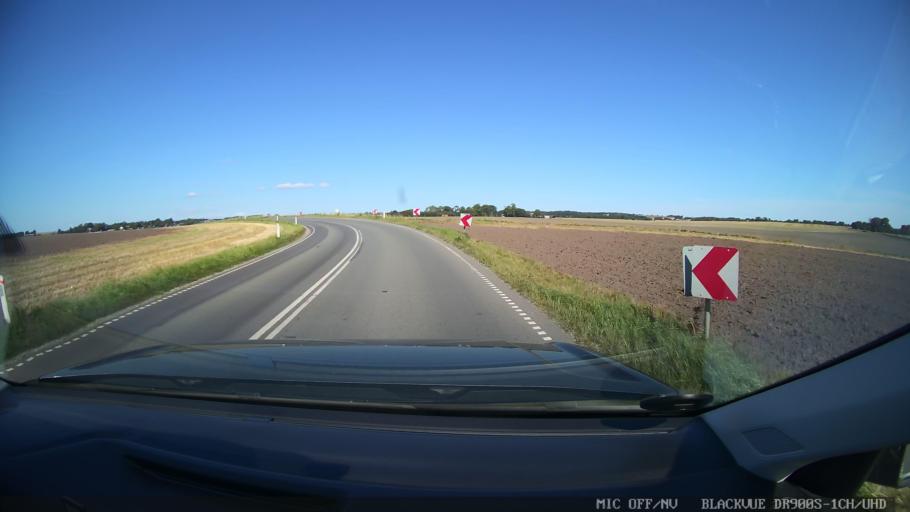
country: DK
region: Central Jutland
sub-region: Randers Kommune
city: Spentrup
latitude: 56.5446
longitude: 10.0017
